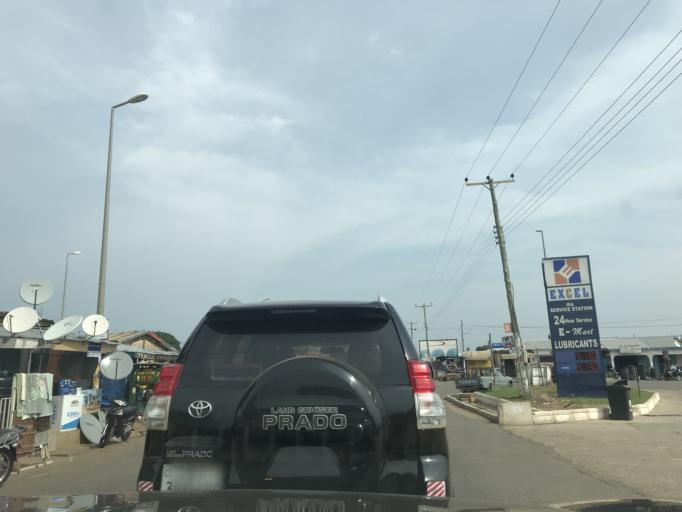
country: GH
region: Upper West
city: Wa
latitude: 10.0697
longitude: -2.5035
